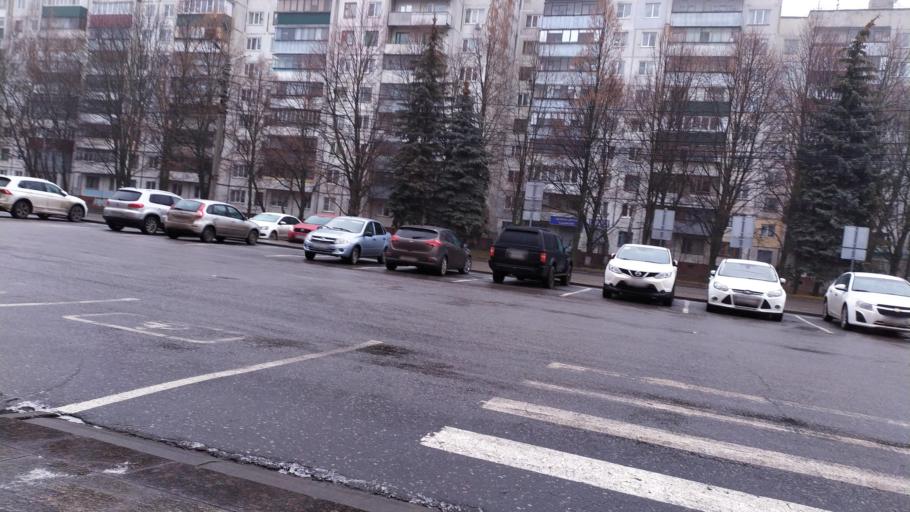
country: RU
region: Kursk
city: Kursk
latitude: 51.7419
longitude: 36.1352
